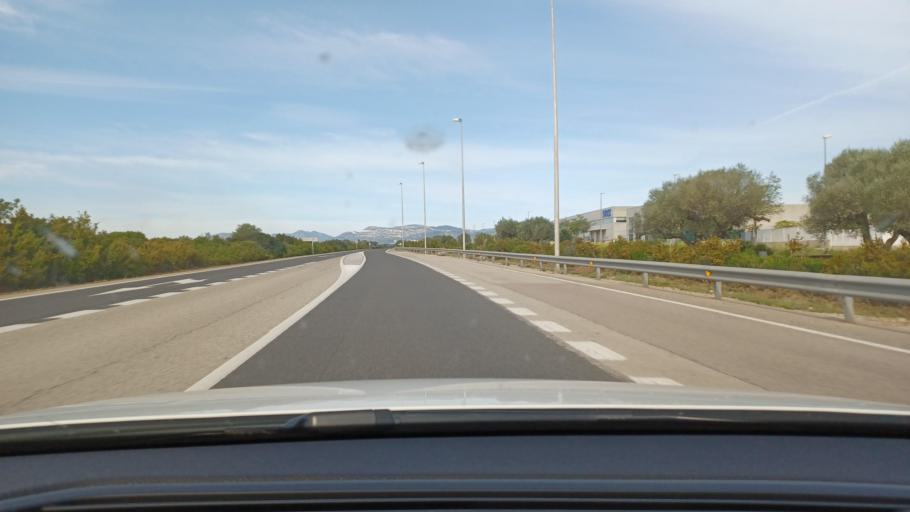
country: ES
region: Catalonia
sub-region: Provincia de Tarragona
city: Mas de Barberans
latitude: 40.6393
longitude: 0.3378
